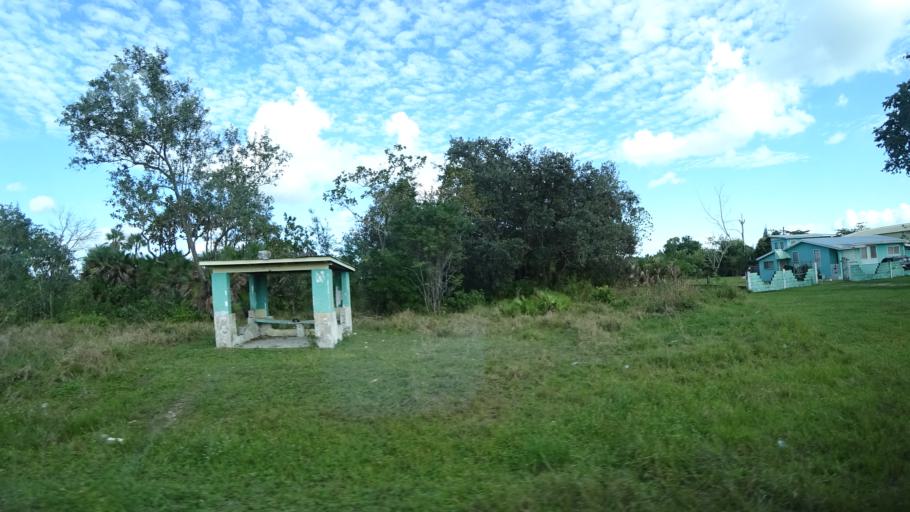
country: BZ
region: Belize
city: Belize City
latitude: 17.5620
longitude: -88.4053
